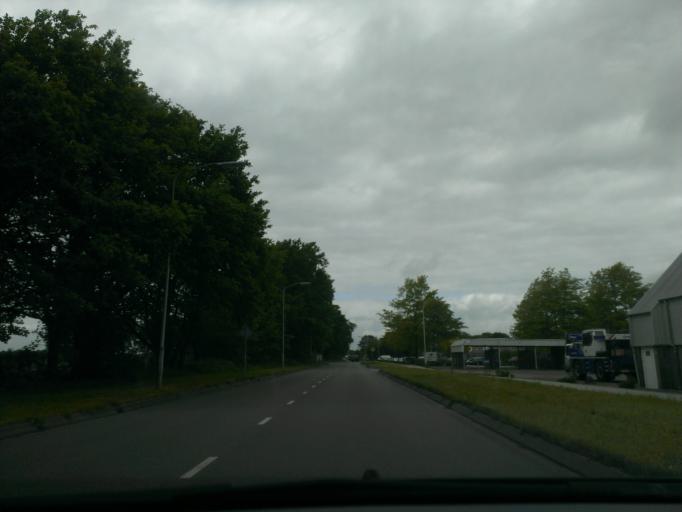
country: NL
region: Drenthe
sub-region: Gemeente Emmen
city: Emmen
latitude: 52.7553
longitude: 6.9143
